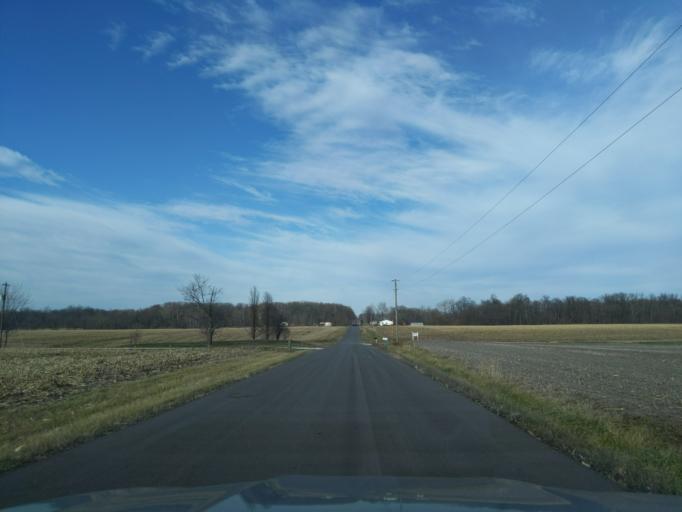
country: US
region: Indiana
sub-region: Decatur County
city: Greensburg
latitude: 39.2219
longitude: -85.4296
